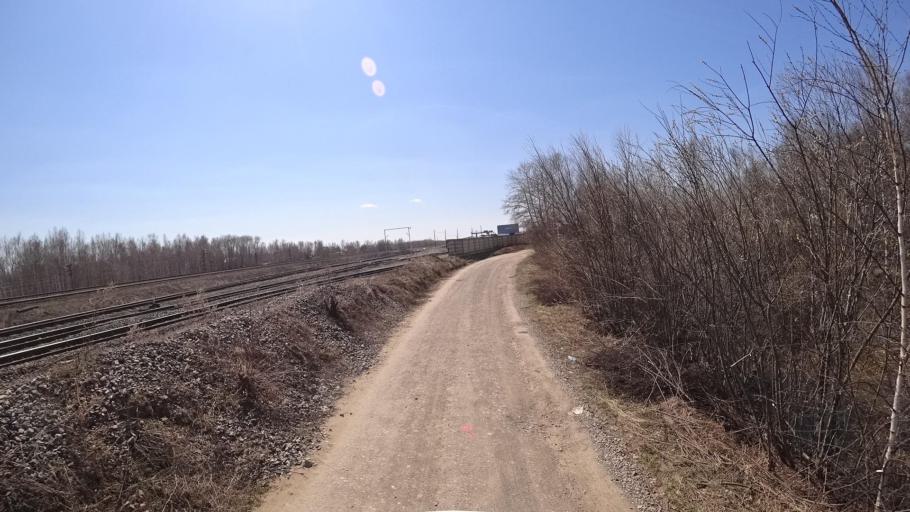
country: RU
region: Khabarovsk Krai
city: Khurba
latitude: 50.4199
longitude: 136.8917
